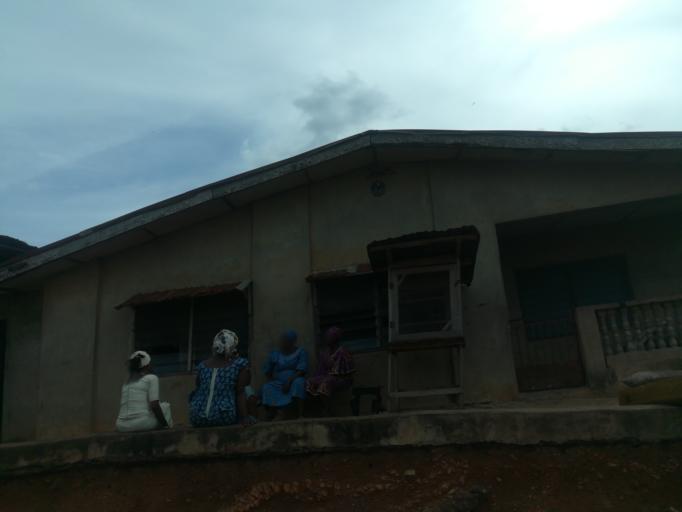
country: NG
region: Oyo
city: Ibadan
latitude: 7.3819
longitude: 3.9438
